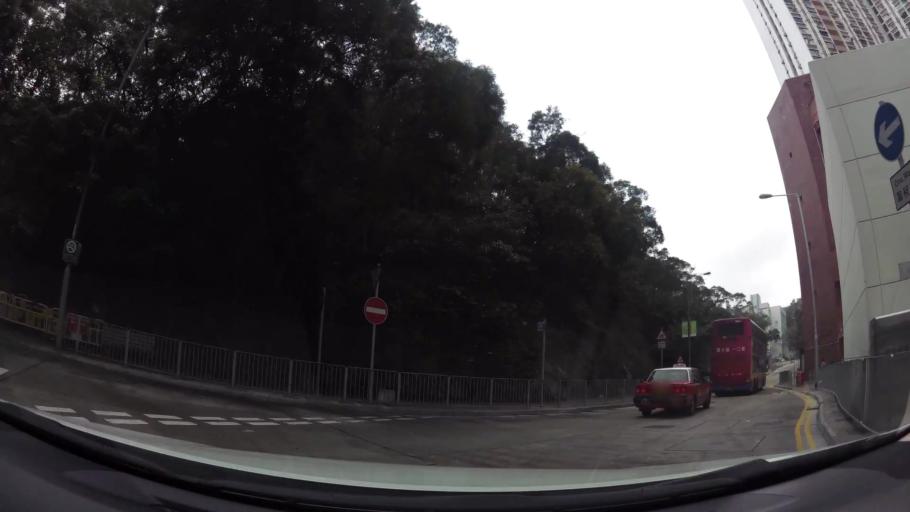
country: HK
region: Central and Western
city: Central
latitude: 22.2407
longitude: 114.1561
